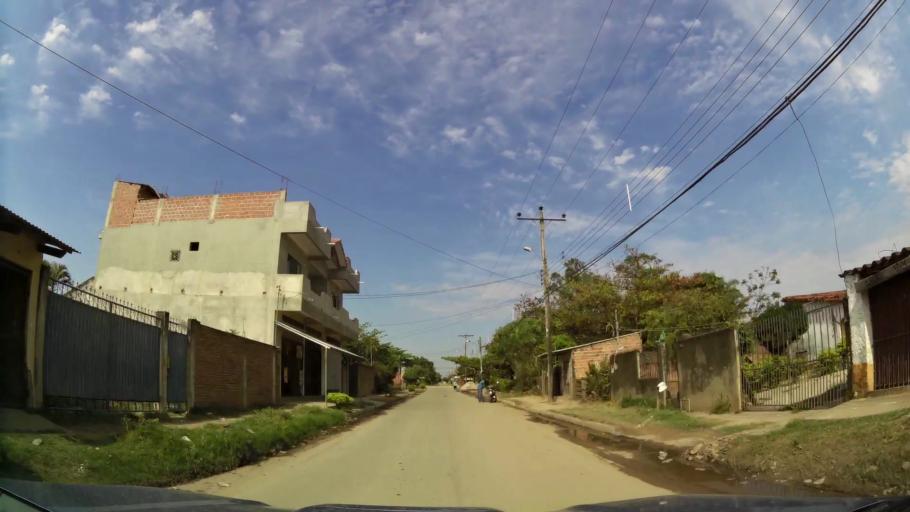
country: BO
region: Santa Cruz
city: Santa Cruz de la Sierra
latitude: -17.7252
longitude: -63.1391
